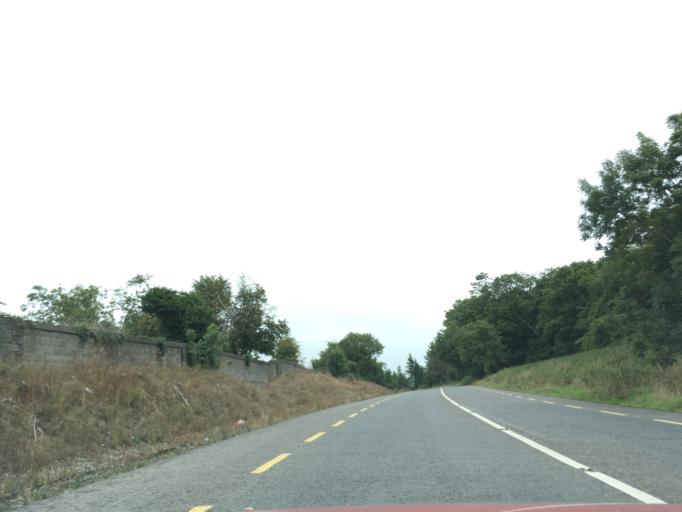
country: IE
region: Munster
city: Carrick-on-Suir
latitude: 52.3656
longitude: -7.5437
